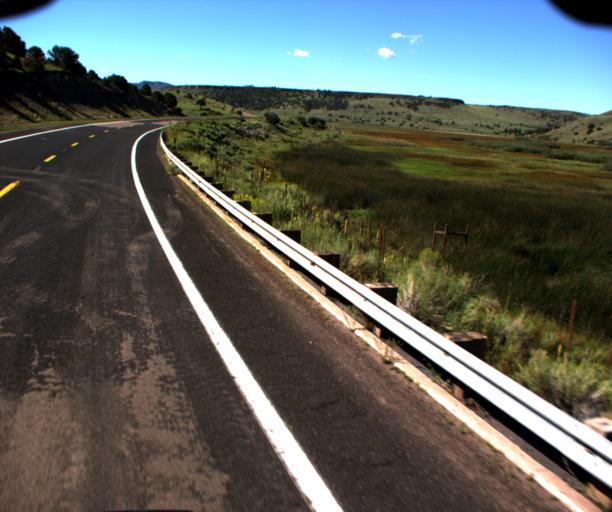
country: US
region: Arizona
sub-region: Apache County
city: Eagar
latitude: 34.0455
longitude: -109.1865
